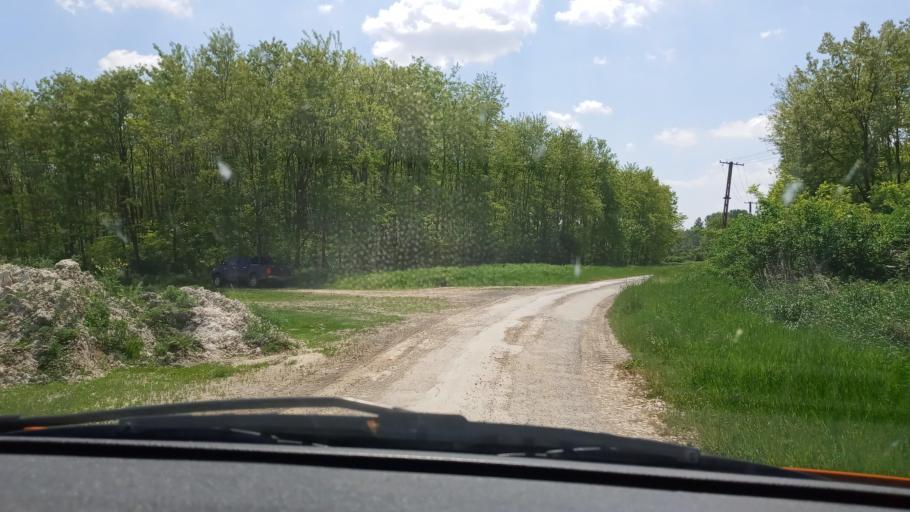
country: HU
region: Baranya
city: Siklos
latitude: 45.7698
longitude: 18.2873
